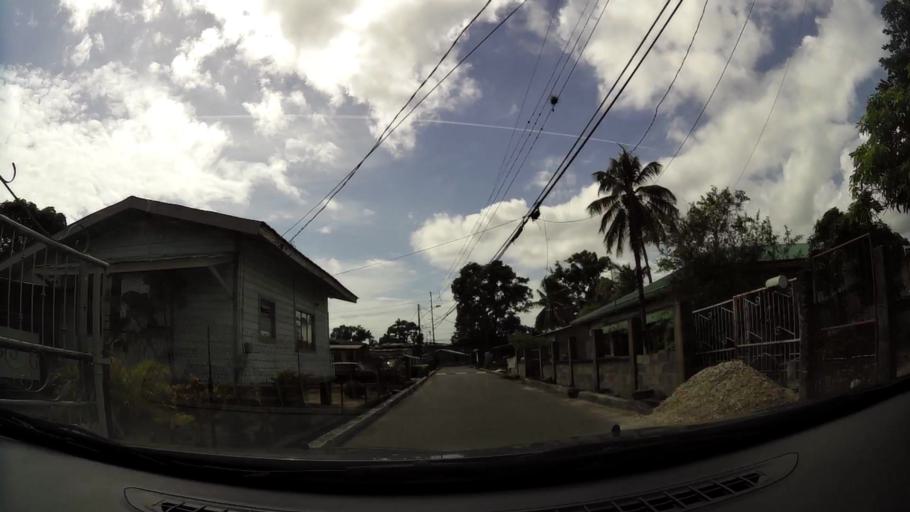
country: TT
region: Borough of Arima
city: Arima
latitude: 10.6311
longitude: -61.2676
